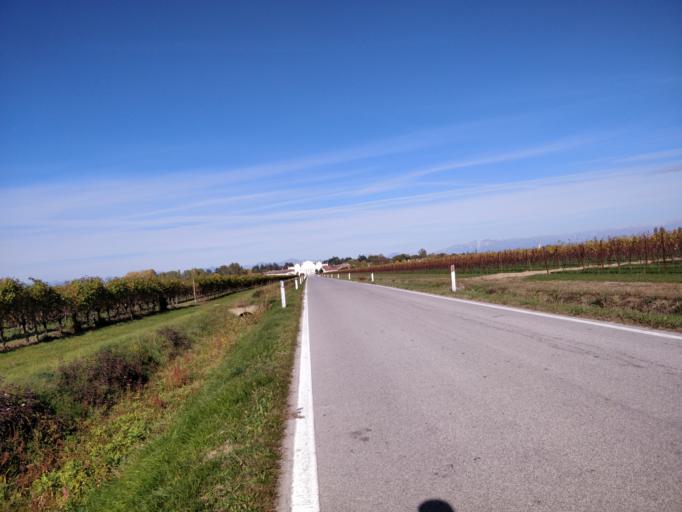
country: IT
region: Friuli Venezia Giulia
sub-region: Provincia di Udine
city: Codroipo
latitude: 45.9400
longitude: 13.0112
